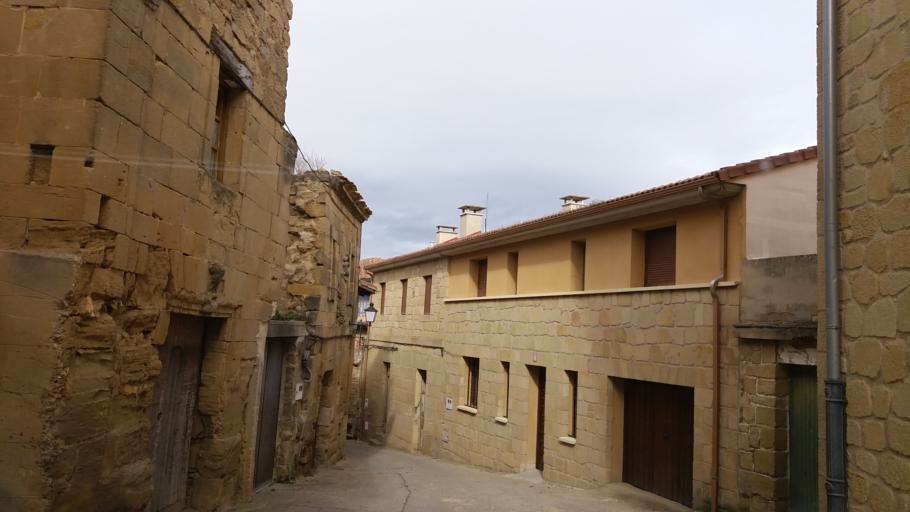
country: ES
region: La Rioja
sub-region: Provincia de La Rioja
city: San Vicente de la Sonsierra
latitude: 42.5611
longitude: -2.7576
